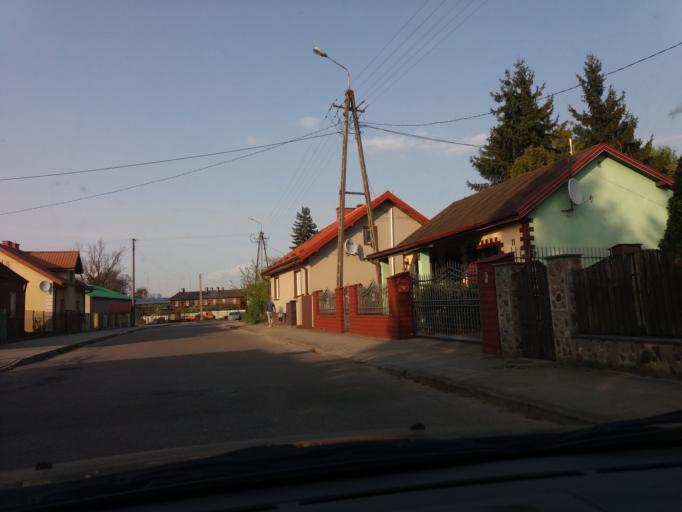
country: PL
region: Masovian Voivodeship
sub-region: Powiat mlawski
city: Mlawa
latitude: 53.1259
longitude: 20.3473
